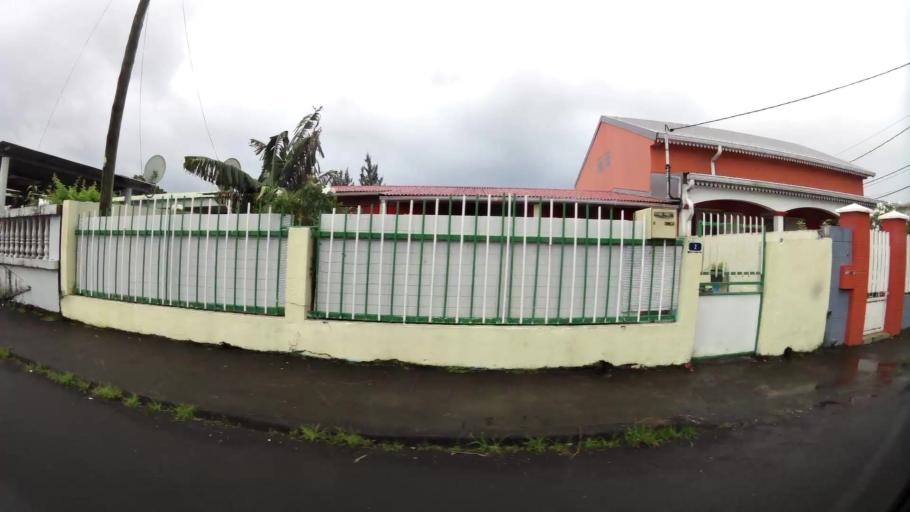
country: RE
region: Reunion
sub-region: Reunion
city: Saint-Andre
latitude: -20.9344
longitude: 55.6503
